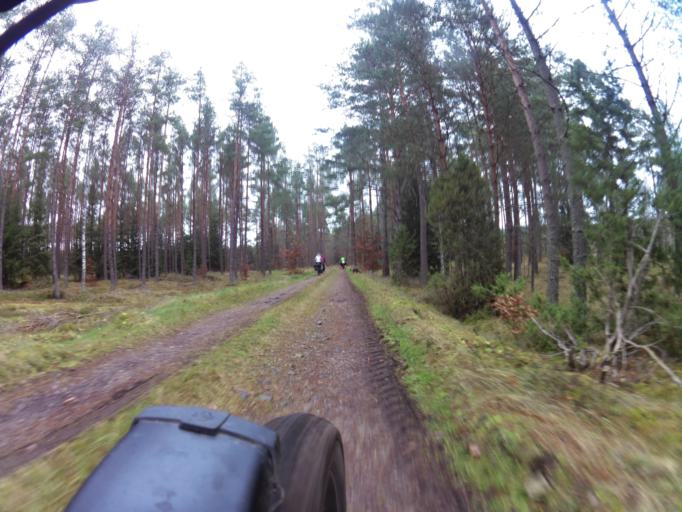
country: PL
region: West Pomeranian Voivodeship
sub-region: Powiat koszalinski
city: Polanow
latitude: 54.0377
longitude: 16.6530
